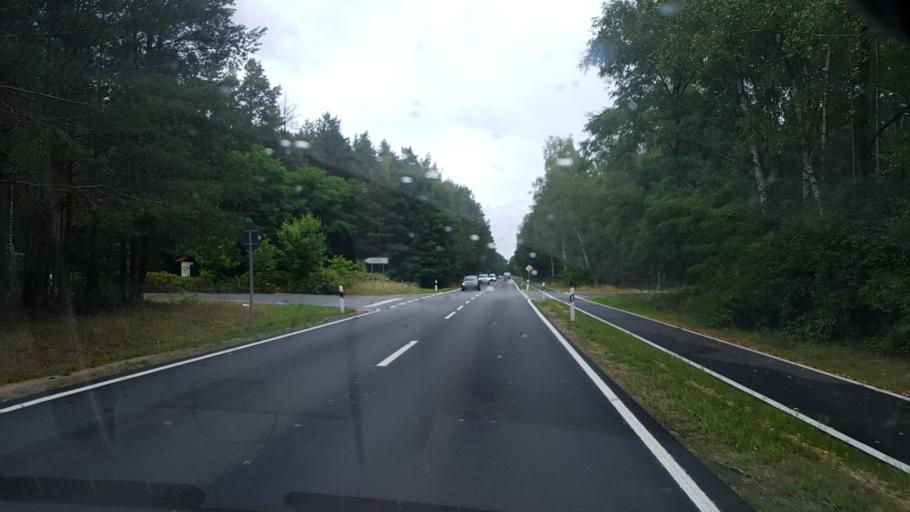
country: DE
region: Saxony
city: Niesky
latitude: 51.3062
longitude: 14.8147
